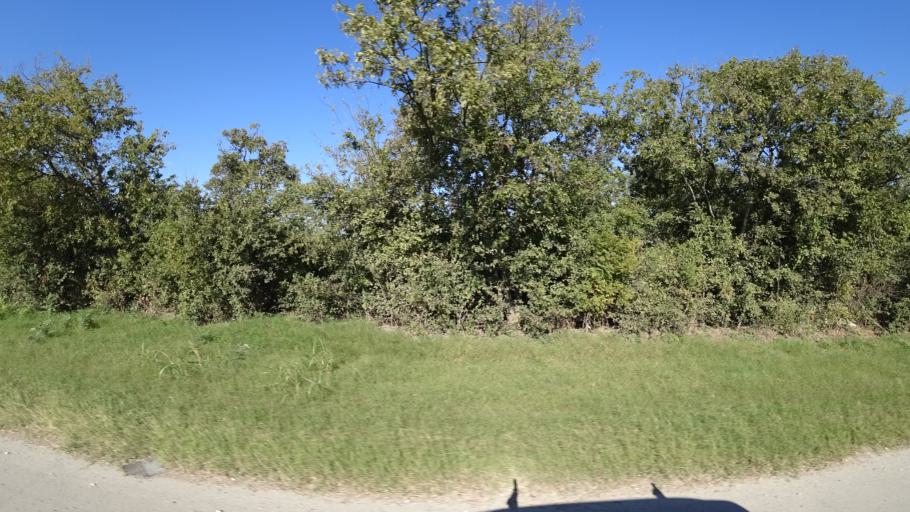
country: US
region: Texas
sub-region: Travis County
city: Hornsby Bend
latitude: 30.2393
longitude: -97.6231
